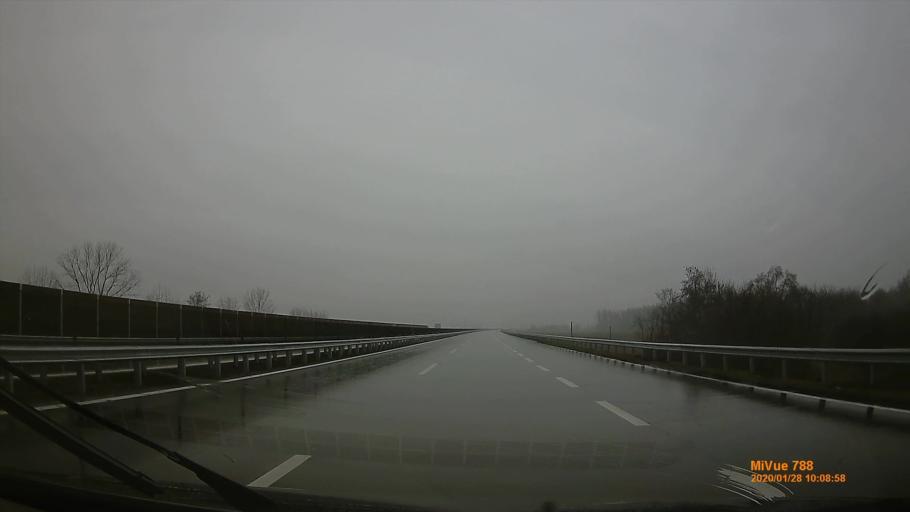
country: HU
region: Pest
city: Pilis
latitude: 47.2894
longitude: 19.5794
